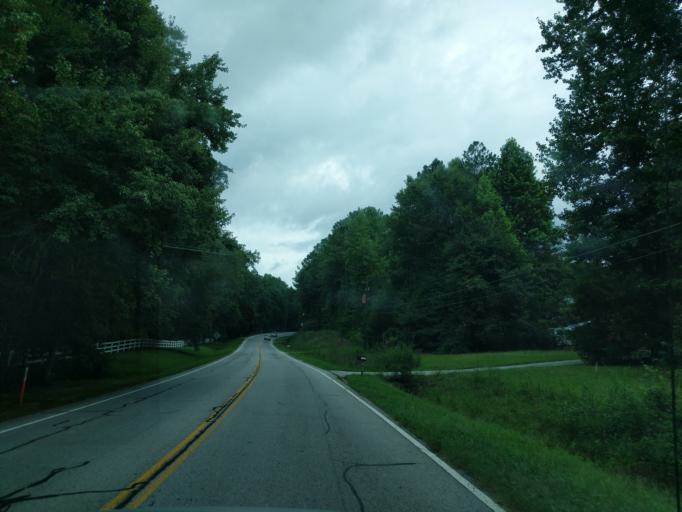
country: US
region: Georgia
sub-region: Walton County
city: Loganville
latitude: 33.8217
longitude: -83.9220
